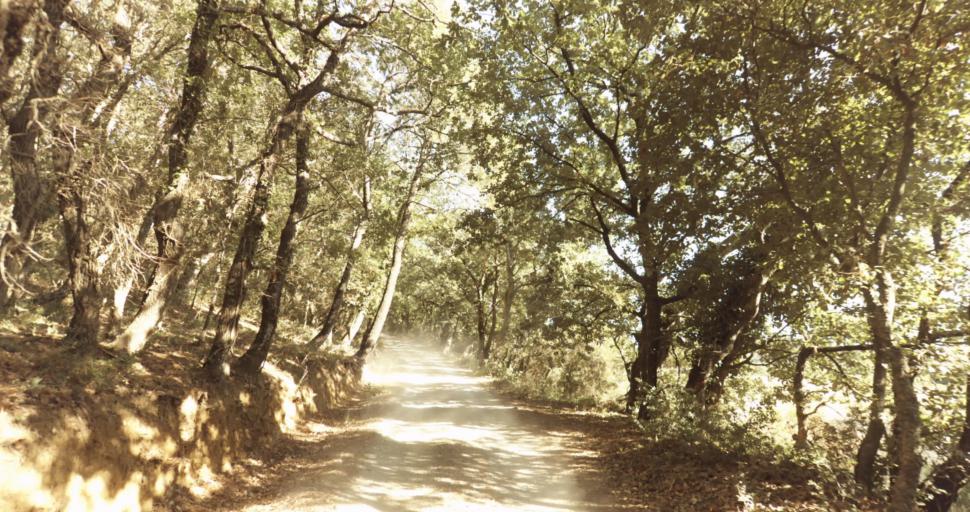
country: FR
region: Provence-Alpes-Cote d'Azur
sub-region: Departement du Var
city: Gassin
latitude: 43.2245
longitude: 6.5803
